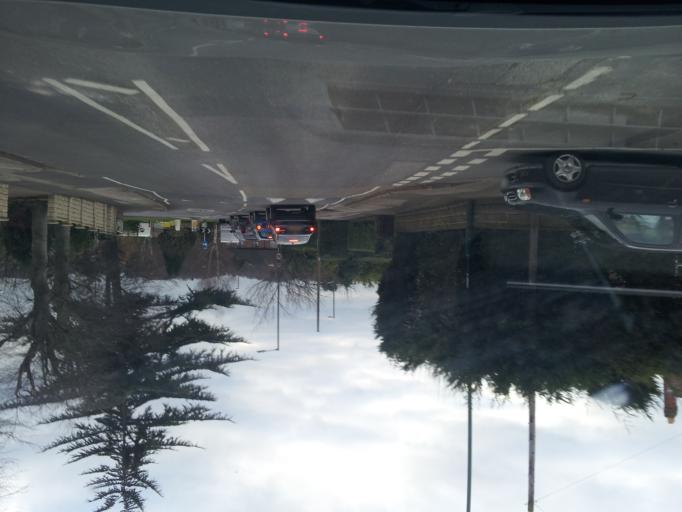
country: GB
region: England
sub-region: Nottinghamshire
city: Kimberley
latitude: 52.9489
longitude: -1.2275
